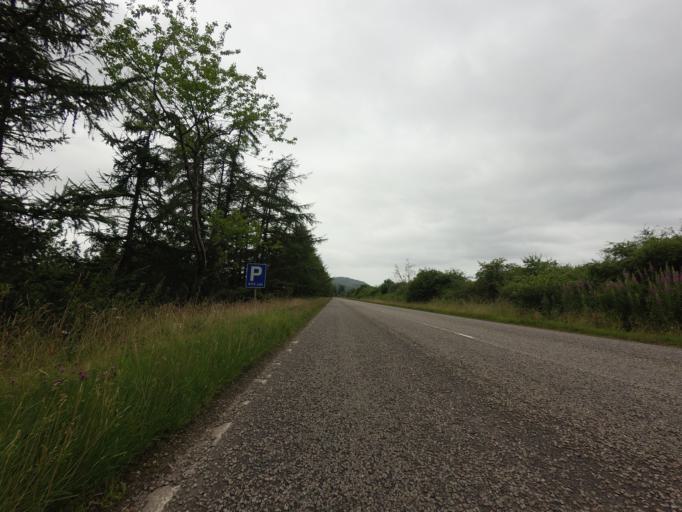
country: GB
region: Scotland
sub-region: Highland
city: Evanton
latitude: 57.9160
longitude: -4.3888
